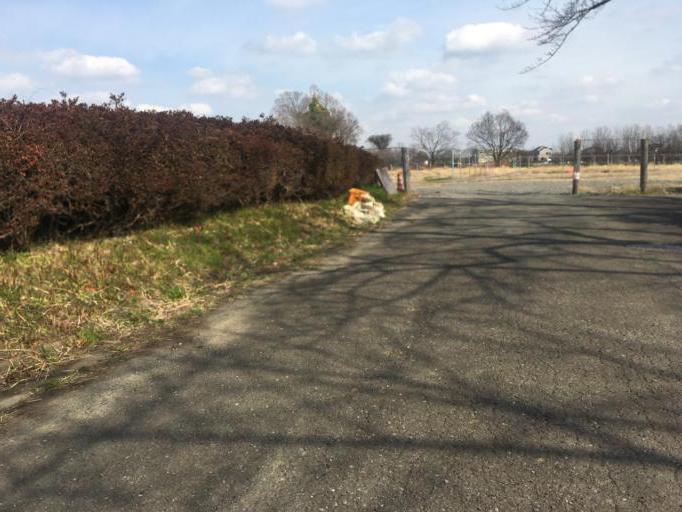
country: JP
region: Saitama
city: Kamifukuoka
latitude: 35.8806
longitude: 139.5562
